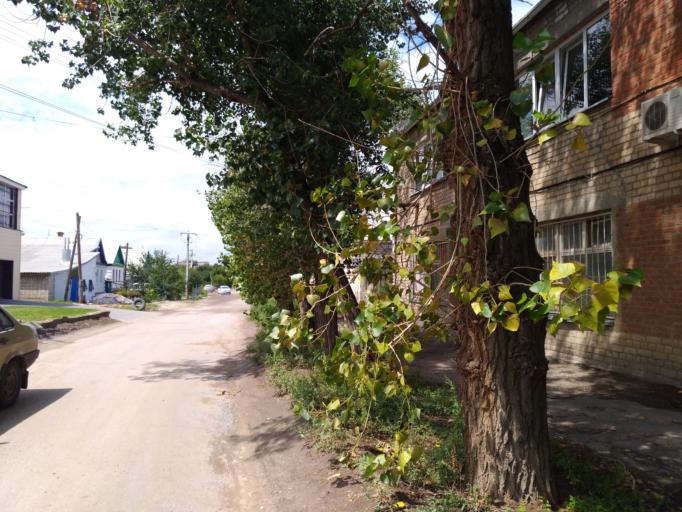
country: RU
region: Volgograd
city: Volgograd
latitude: 48.7111
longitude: 44.4628
